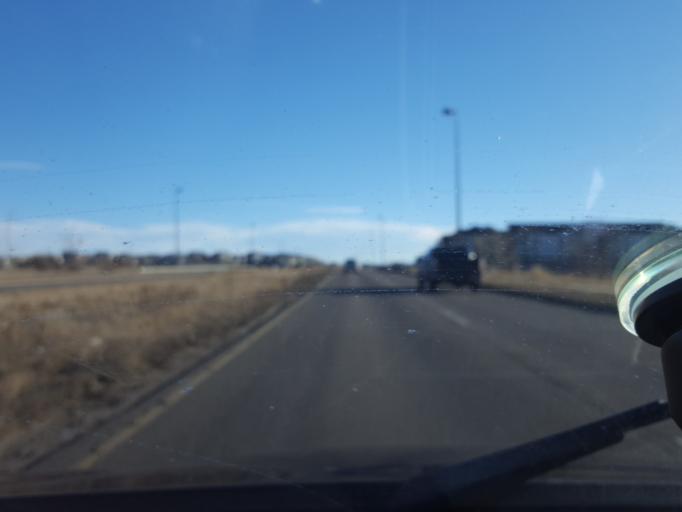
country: US
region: Colorado
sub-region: Adams County
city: Aurora
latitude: 39.7967
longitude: -104.7722
